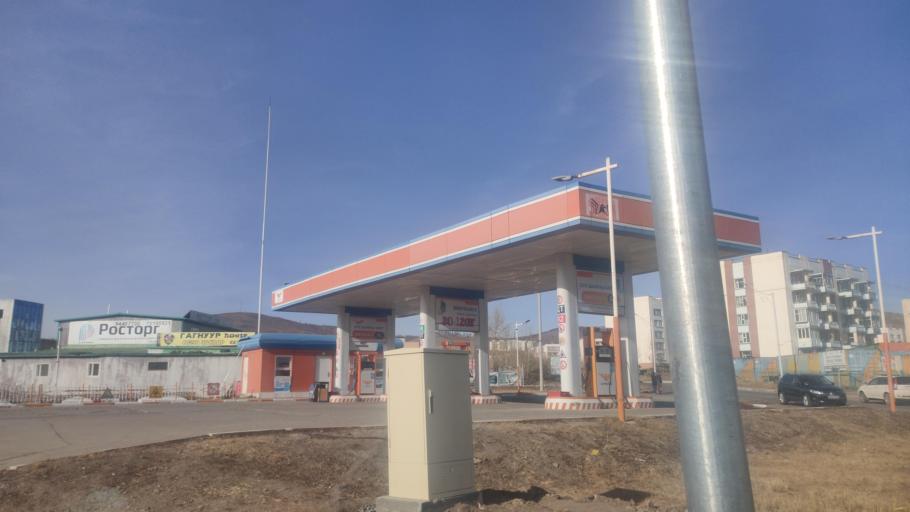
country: MN
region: Orhon
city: Erdenet
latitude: 49.0244
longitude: 104.0609
